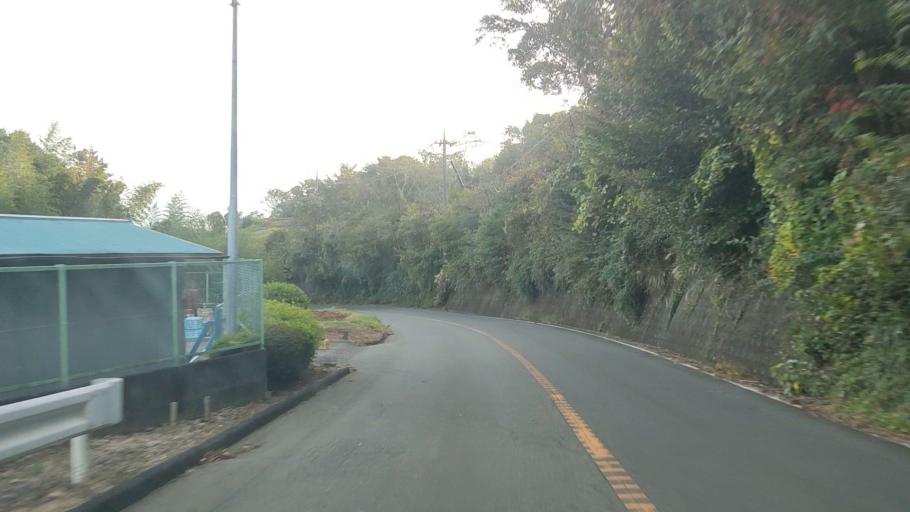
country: JP
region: Shizuoka
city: Mishima
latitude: 35.1546
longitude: 138.9277
